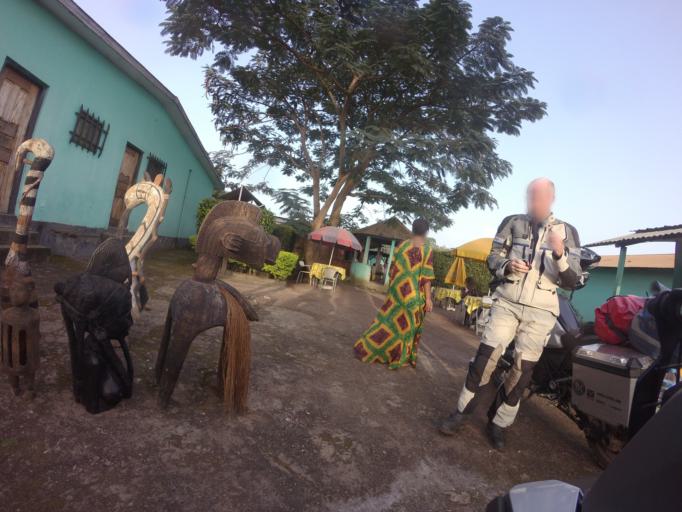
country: GN
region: Nzerekore
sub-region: Nzerekore Prefecture
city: Nzerekore
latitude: 7.7668
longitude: -8.8206
